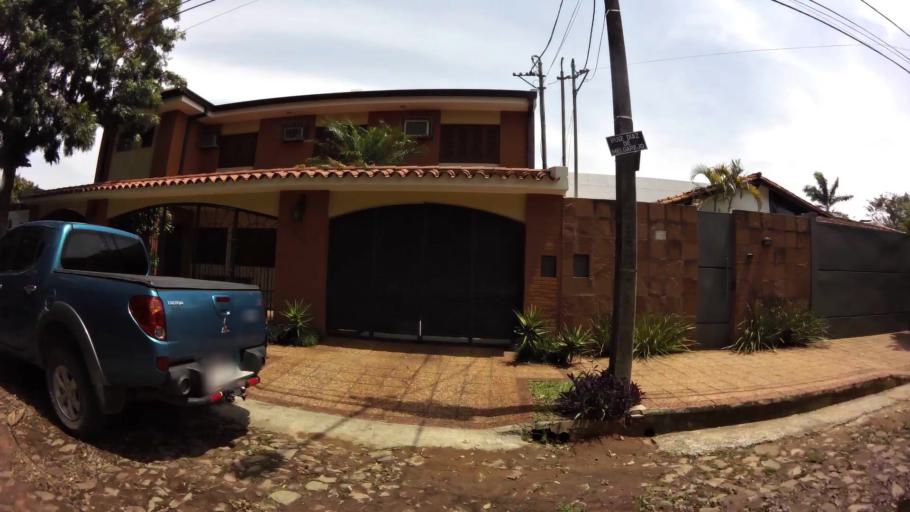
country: PY
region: Central
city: Lambare
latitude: -25.3103
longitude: -57.5834
